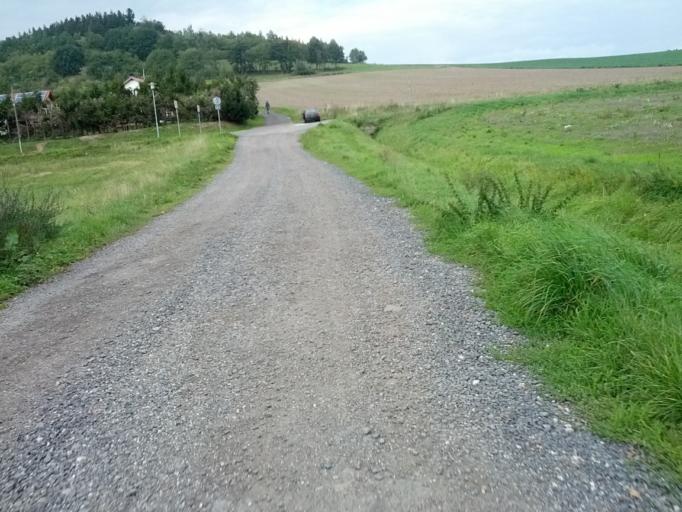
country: DE
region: Thuringia
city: Seebach
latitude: 50.9393
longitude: 10.4064
